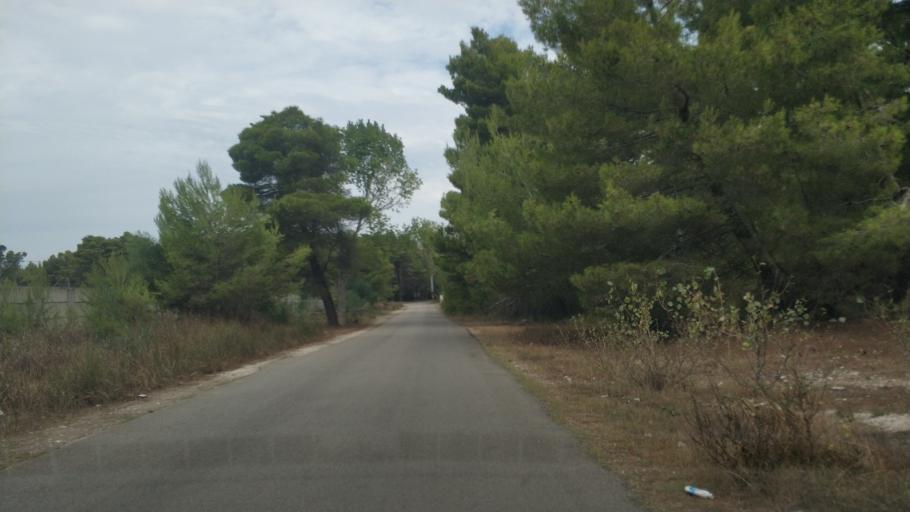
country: AL
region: Vlore
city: Vlore
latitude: 40.4911
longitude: 19.4380
